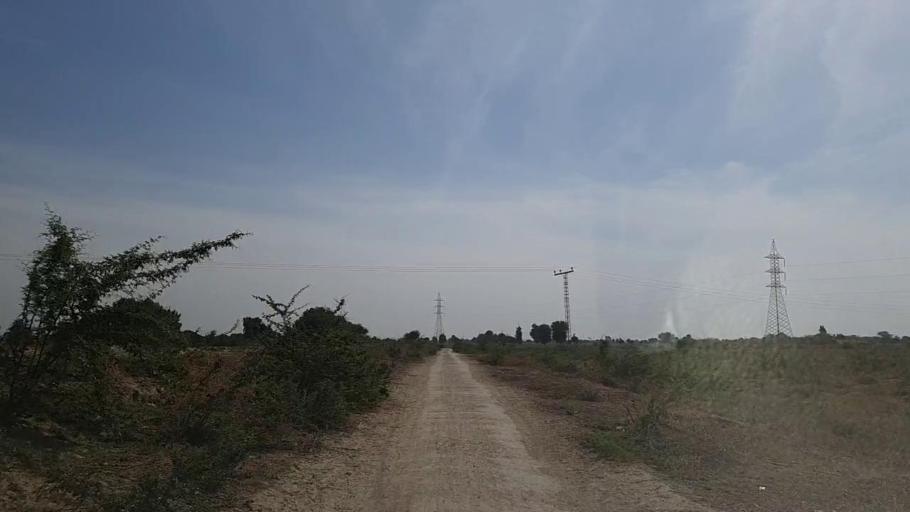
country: PK
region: Sindh
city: Samaro
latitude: 25.2094
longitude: 69.4564
